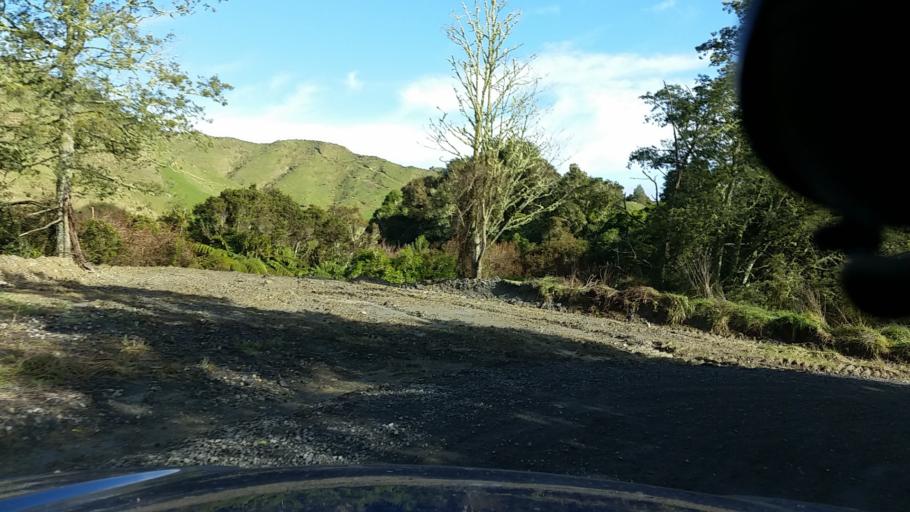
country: NZ
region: Taranaki
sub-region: New Plymouth District
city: Waitara
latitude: -39.0614
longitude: 174.7905
